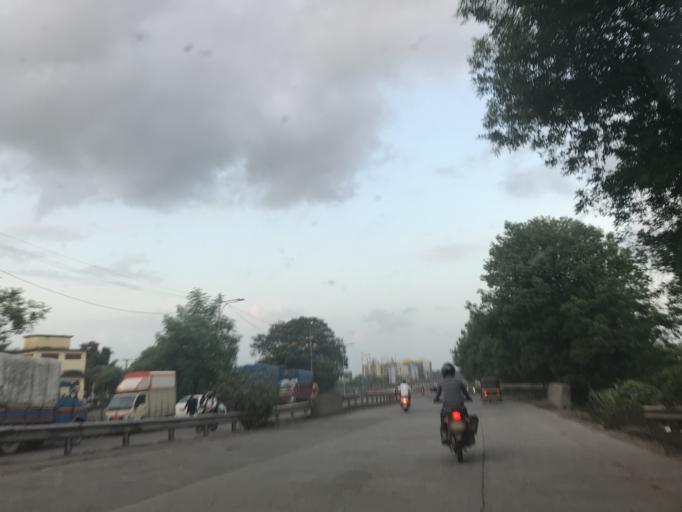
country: IN
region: Maharashtra
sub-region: Thane
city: Thane
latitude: 19.2225
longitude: 72.9912
